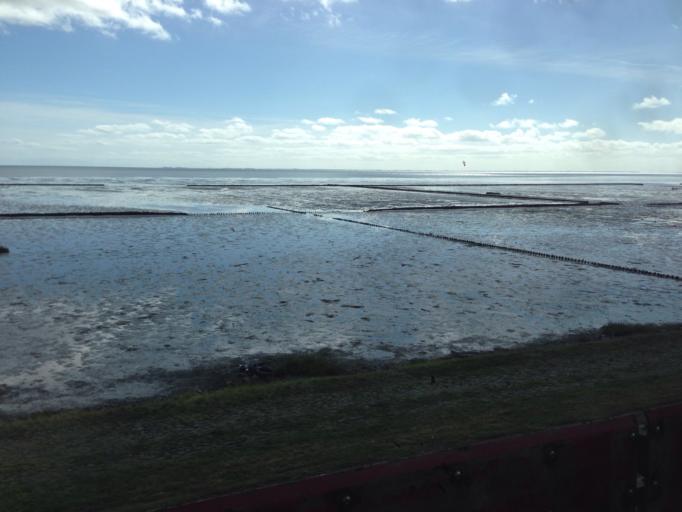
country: DE
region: Schleswig-Holstein
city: Sylt-Ost
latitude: 54.8762
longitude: 8.4891
